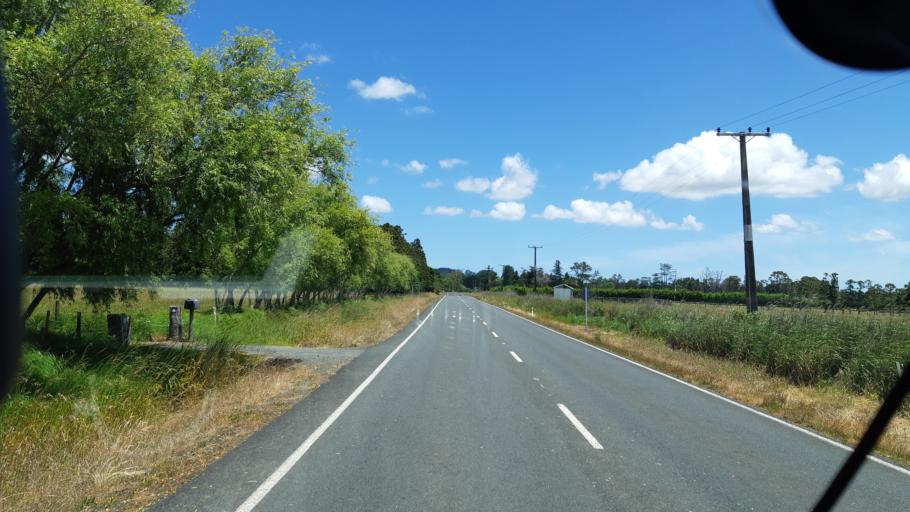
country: NZ
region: Northland
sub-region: Far North District
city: Kaitaia
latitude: -35.1387
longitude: 173.3612
